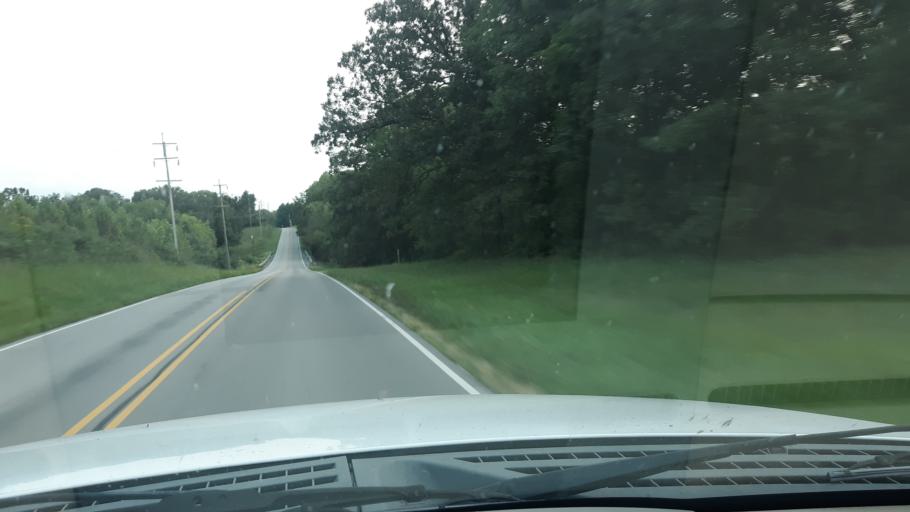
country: US
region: Illinois
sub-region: White County
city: Norris City
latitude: 37.9287
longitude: -88.3484
